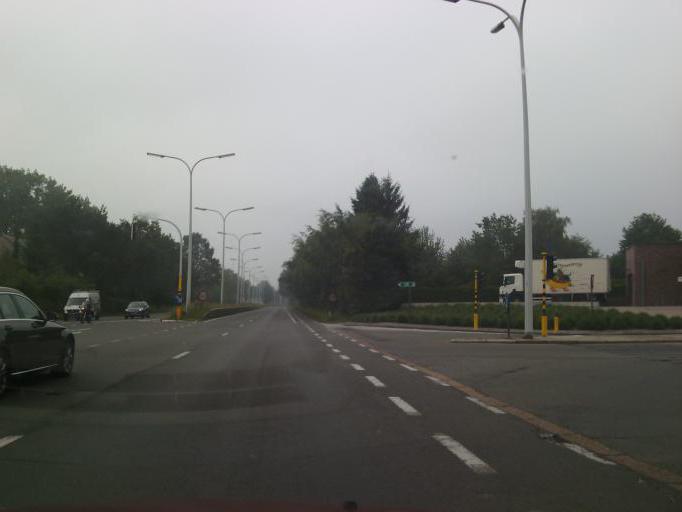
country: BE
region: Flanders
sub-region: Provincie Oost-Vlaanderen
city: Aalst
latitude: 50.9649
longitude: 4.0384
